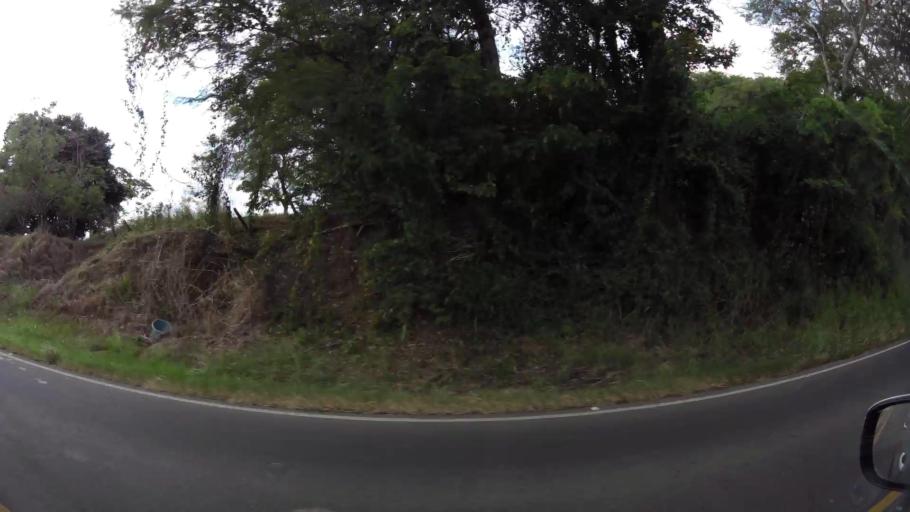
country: CR
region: Guanacaste
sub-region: Canton de Nicoya
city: Nicoya
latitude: 10.1569
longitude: -85.3074
